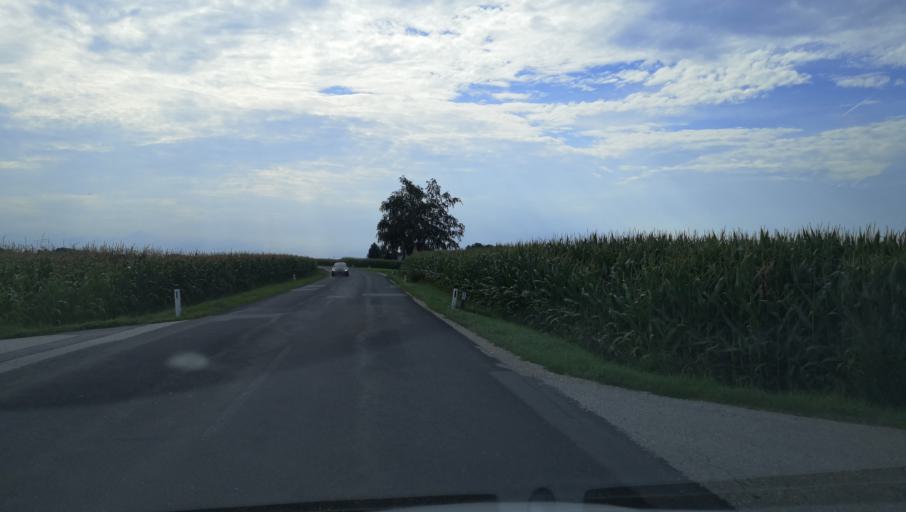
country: AT
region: Lower Austria
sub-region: Politischer Bezirk Amstetten
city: Amstetten
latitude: 48.1474
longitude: 14.8680
